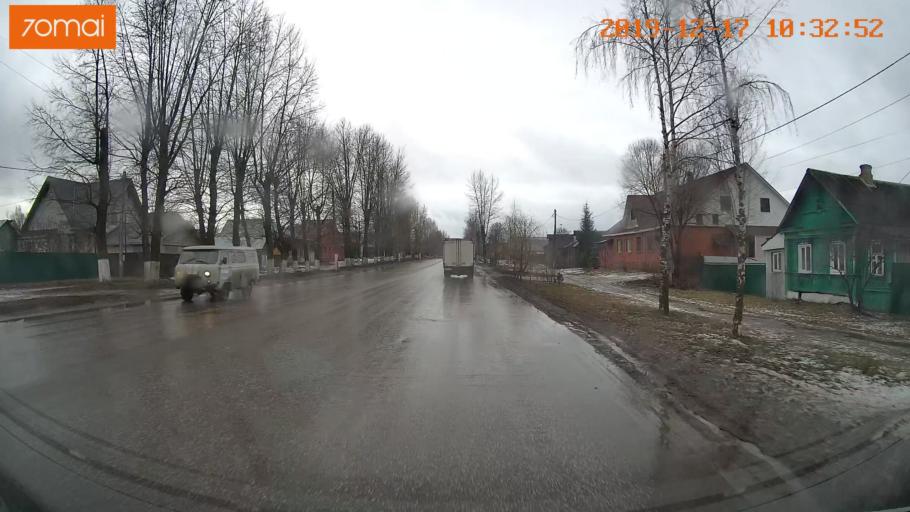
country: RU
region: Vladimir
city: Gus'-Khrustal'nyy
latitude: 55.6262
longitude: 40.6854
